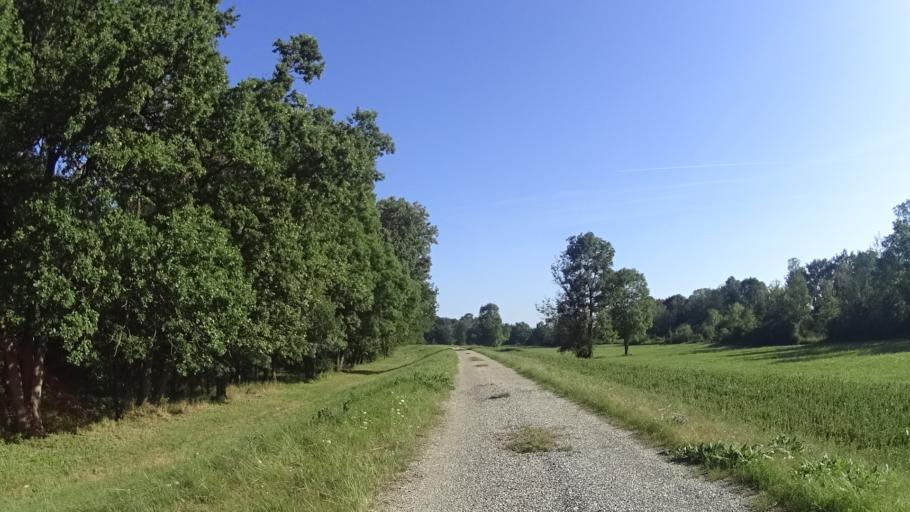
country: CZ
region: South Moravian
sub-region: Okres Breclav
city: Lanzhot
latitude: 48.6708
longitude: 16.9844
